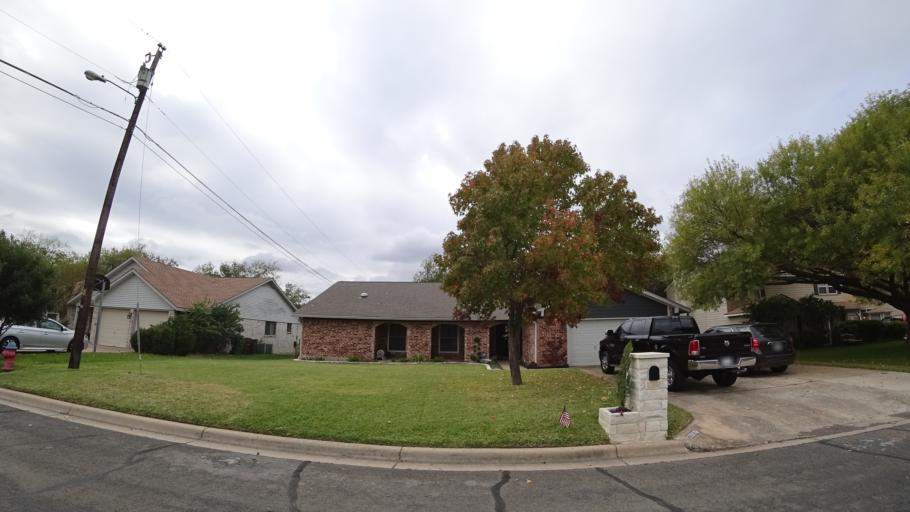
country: US
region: Texas
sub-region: Williamson County
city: Round Rock
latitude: 30.4899
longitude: -97.7025
